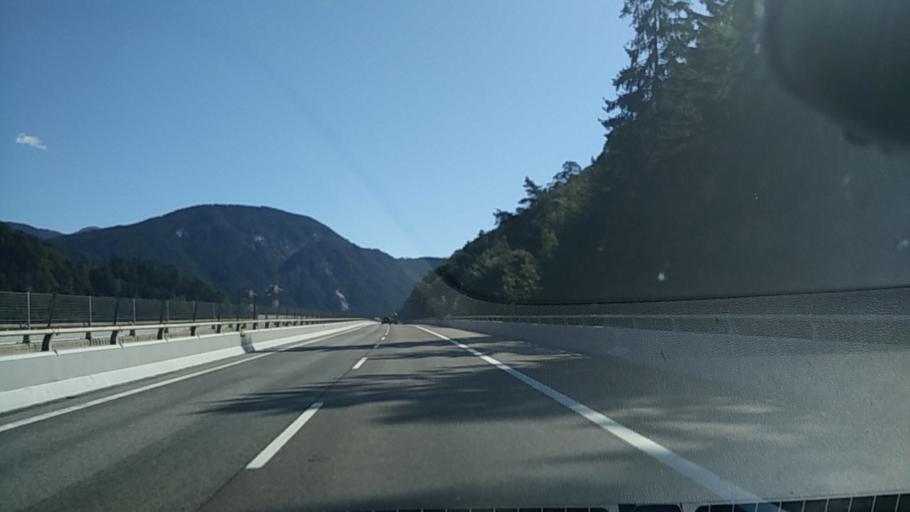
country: IT
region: Friuli Venezia Giulia
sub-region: Provincia di Udine
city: Malborghetto
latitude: 46.5028
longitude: 13.4419
